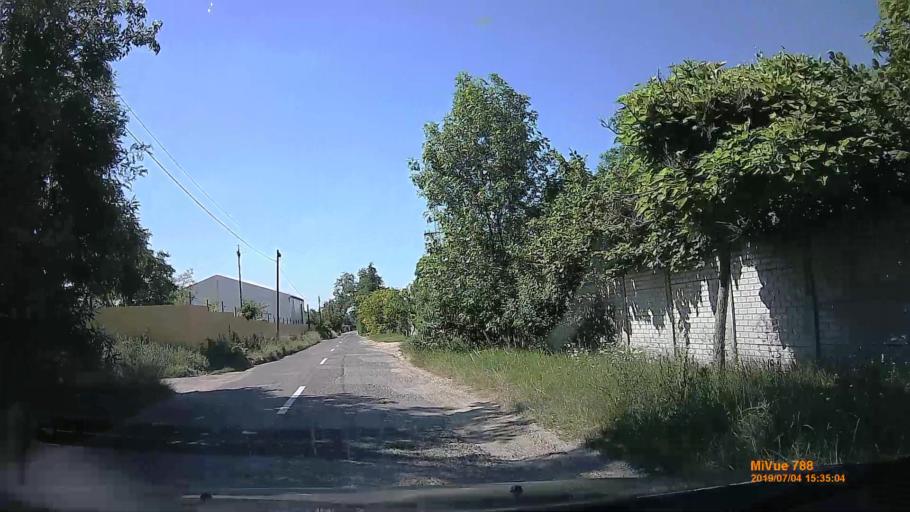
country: HU
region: Komarom-Esztergom
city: Tatabanya
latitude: 47.5397
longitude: 18.3865
